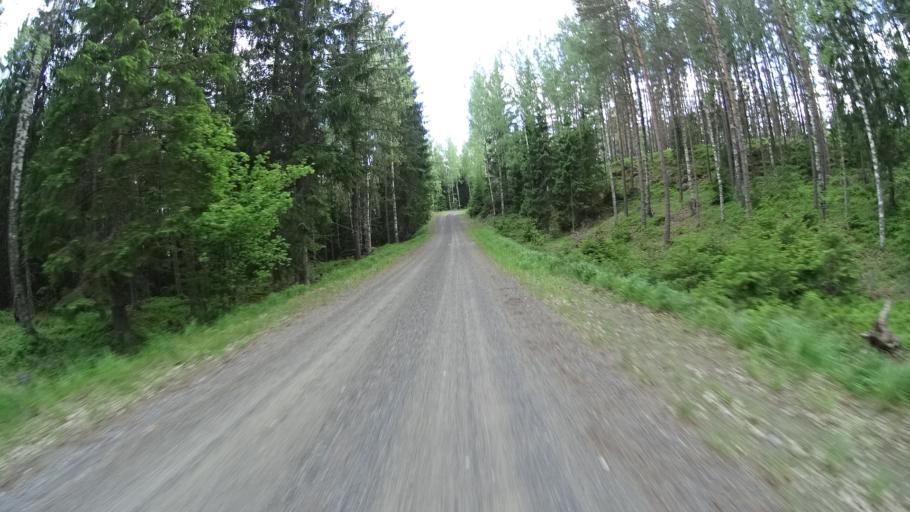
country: FI
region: Uusimaa
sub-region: Raaseporin
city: Pohja
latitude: 60.1791
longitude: 23.5541
